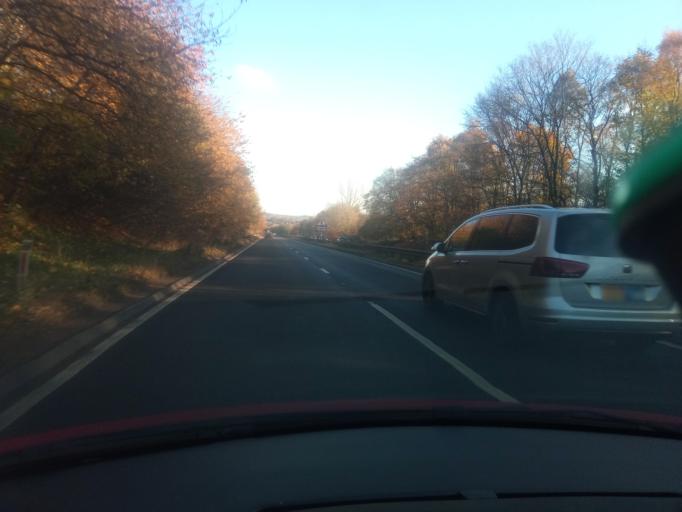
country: GB
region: England
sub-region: Derbyshire
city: Blackwell
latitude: 53.0933
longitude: -1.3441
